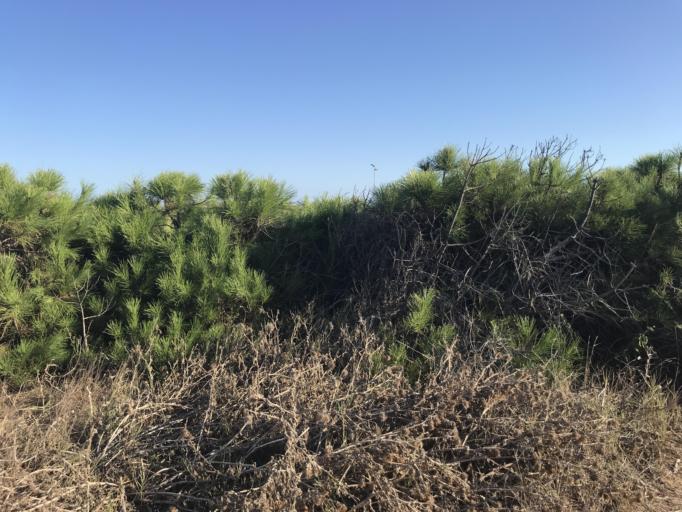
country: ES
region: Valencia
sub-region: Provincia de Alicante
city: Torrevieja
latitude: 38.0302
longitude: -0.6518
